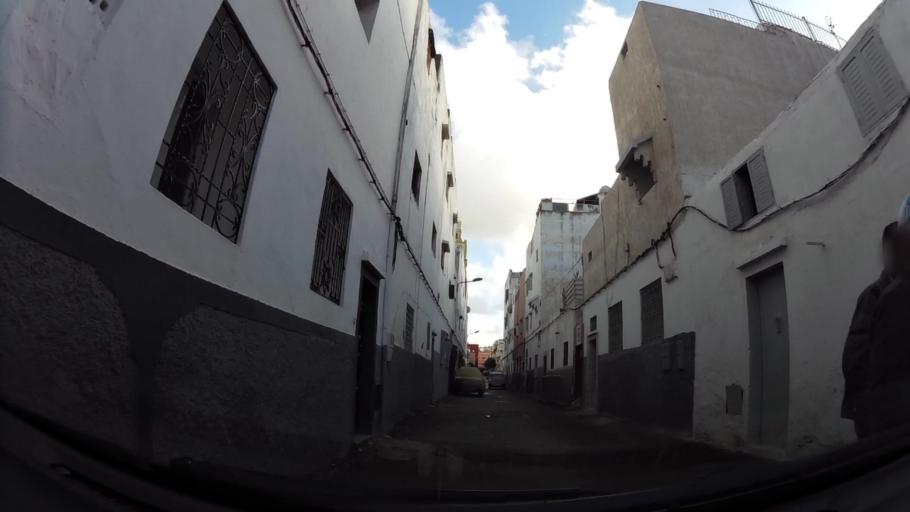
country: MA
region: Grand Casablanca
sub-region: Casablanca
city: Casablanca
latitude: 33.5532
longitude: -7.5934
